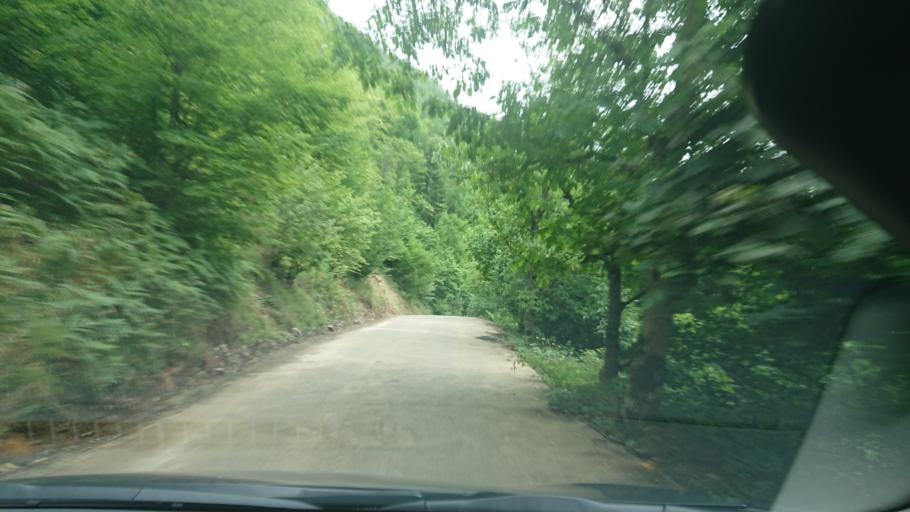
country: TR
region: Gumushane
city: Kurtun
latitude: 40.6776
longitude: 39.0449
